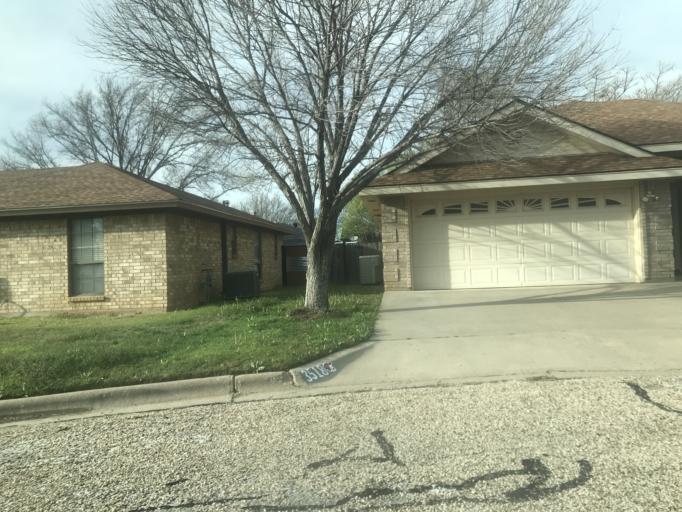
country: US
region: Texas
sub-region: Taylor County
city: Abilene
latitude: 32.3966
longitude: -99.7685
